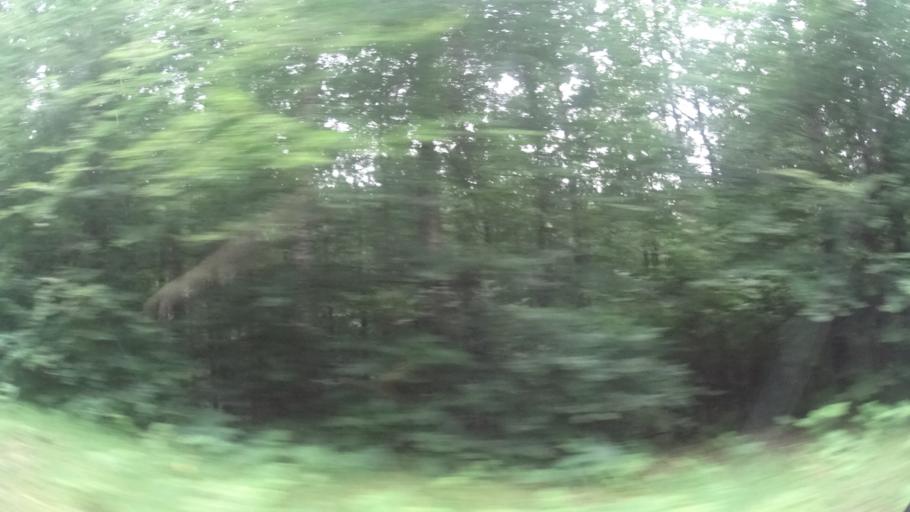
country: DE
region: Hesse
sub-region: Regierungsbezirk Darmstadt
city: Steinau an der Strasse
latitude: 50.2488
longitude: 9.4470
